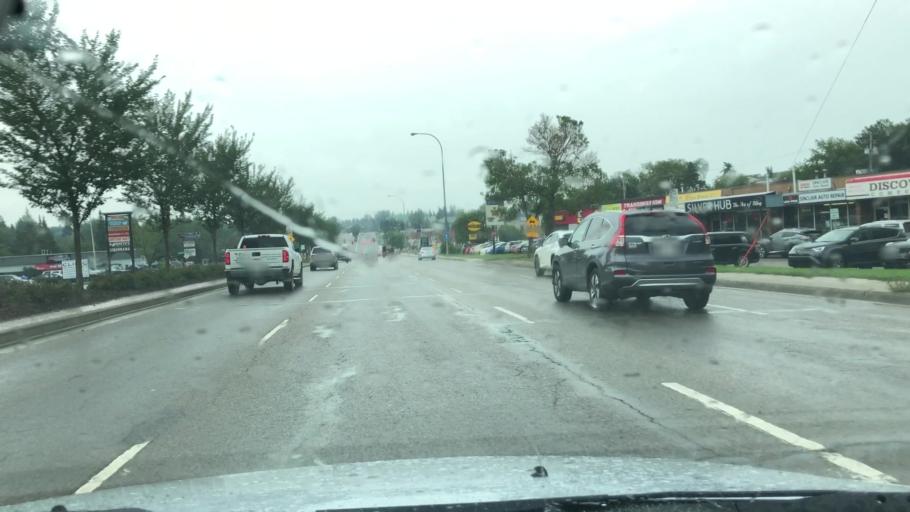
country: CA
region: Alberta
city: St. Albert
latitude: 53.6388
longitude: -113.6246
